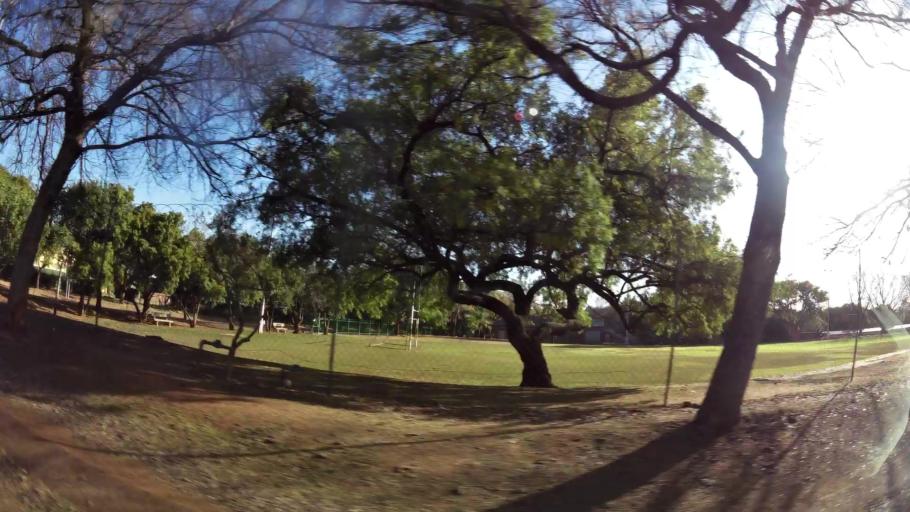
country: ZA
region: Gauteng
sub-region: City of Tshwane Metropolitan Municipality
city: Pretoria
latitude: -25.7312
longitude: 28.2076
